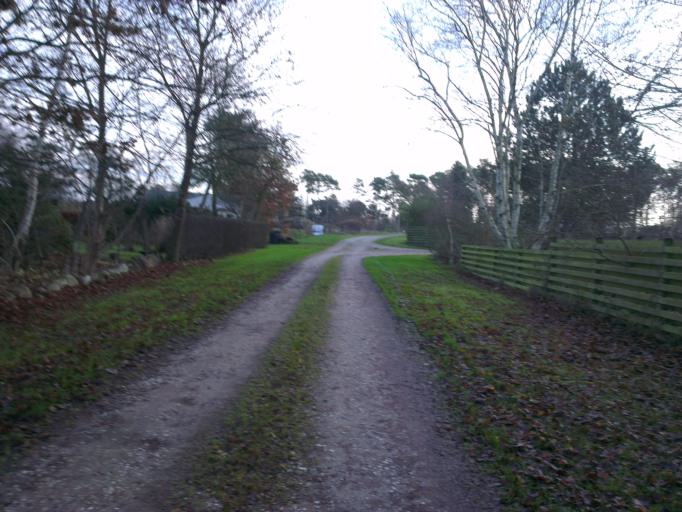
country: DK
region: Capital Region
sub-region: Frederikssund Kommune
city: Jaegerspris
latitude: 55.8417
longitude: 11.9600
